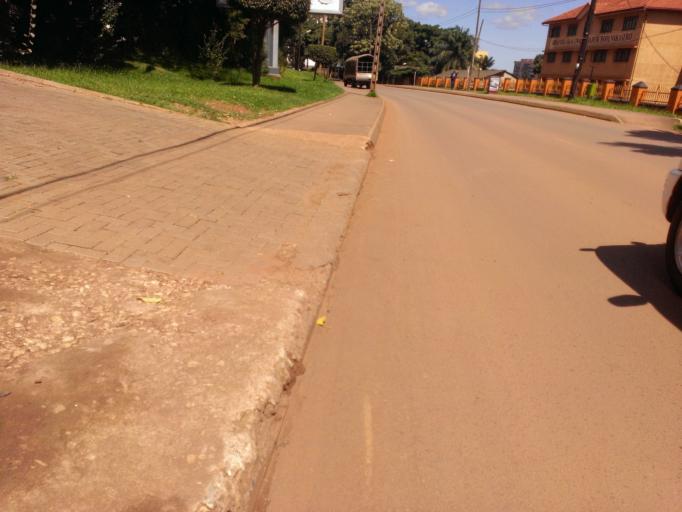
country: UG
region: Central Region
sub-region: Kampala District
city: Kampala
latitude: 0.3195
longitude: 32.5786
